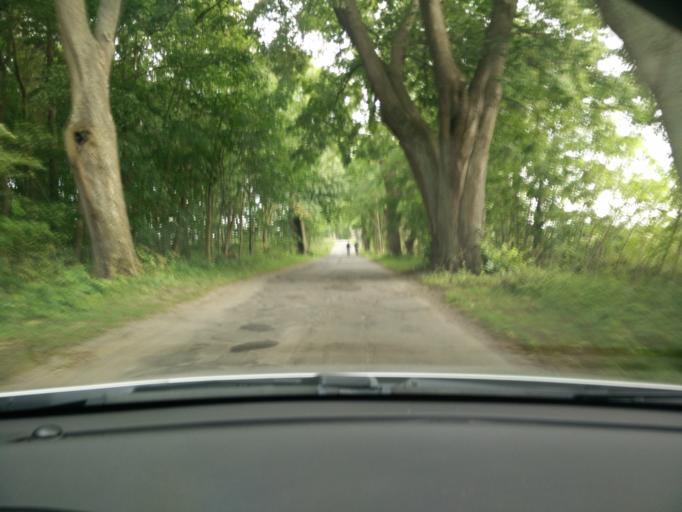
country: PL
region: Pomeranian Voivodeship
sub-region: Powiat pucki
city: Mrzezino
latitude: 54.6769
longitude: 18.4593
